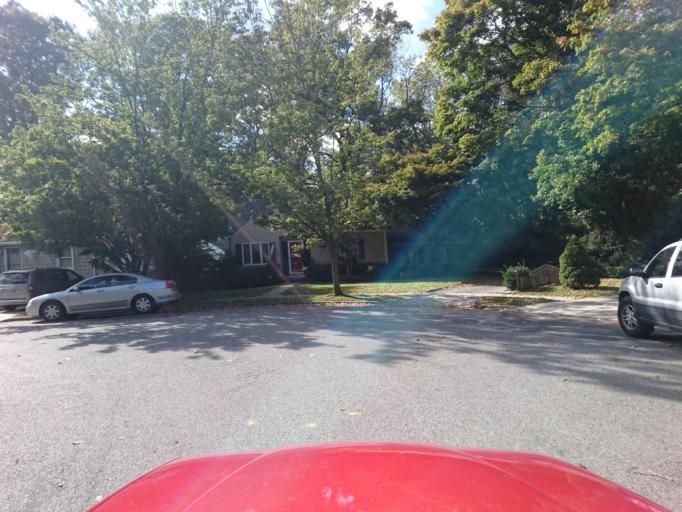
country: US
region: New York
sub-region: Nassau County
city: Glen Cove
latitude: 40.8762
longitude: -73.6333
